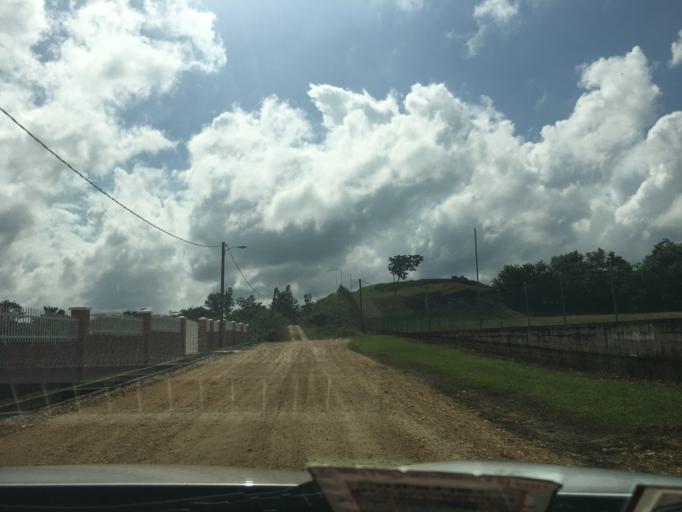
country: BZ
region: Cayo
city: Belmopan
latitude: 17.2498
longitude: -88.7884
